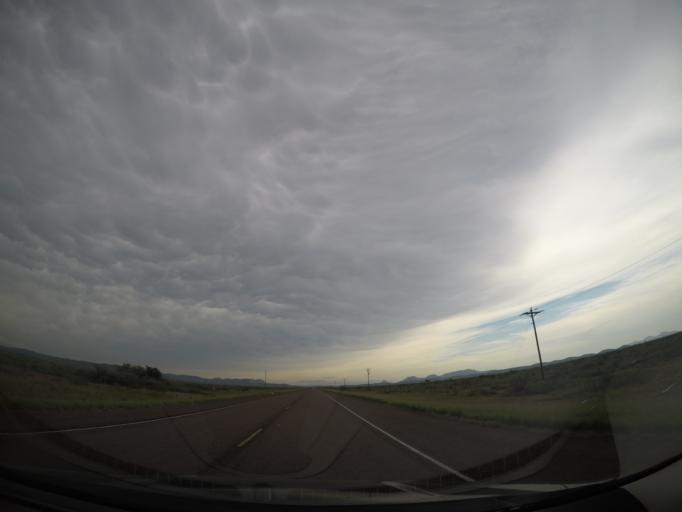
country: US
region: Texas
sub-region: Brewster County
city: Alpine
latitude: 30.2128
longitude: -103.0793
